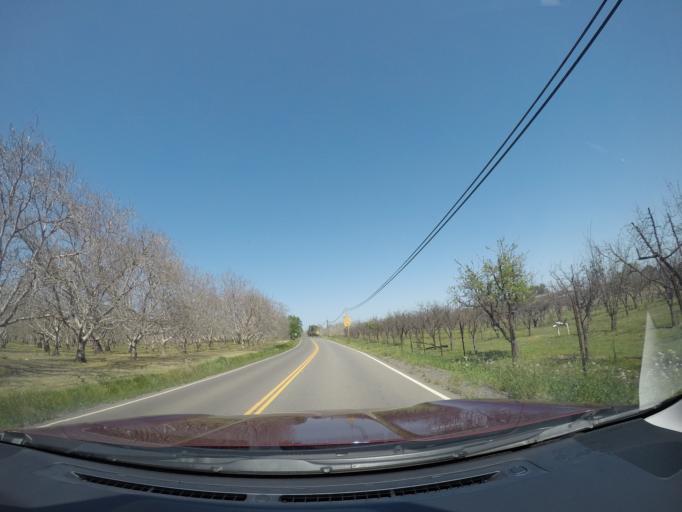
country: US
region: California
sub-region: Yolo County
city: Winters
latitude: 38.4939
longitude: -121.9512
